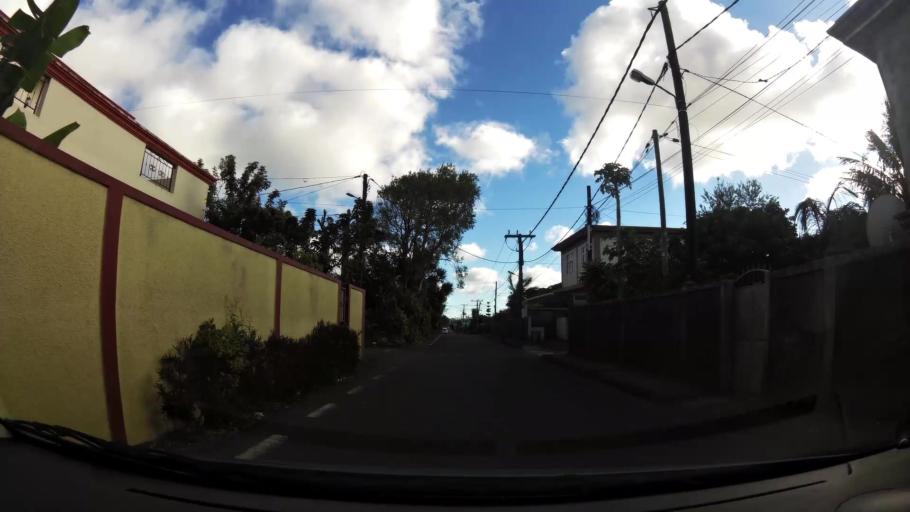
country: MU
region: Plaines Wilhems
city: Curepipe
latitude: -20.2954
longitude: 57.5152
